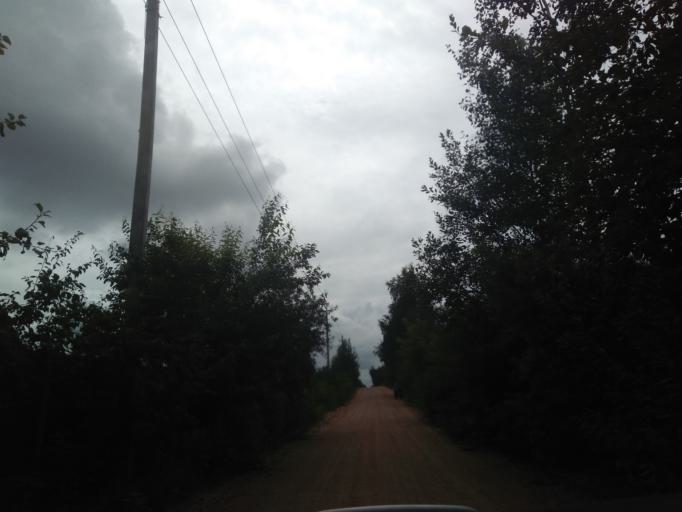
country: BY
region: Minsk
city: Slabada
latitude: 53.9897
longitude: 27.9115
